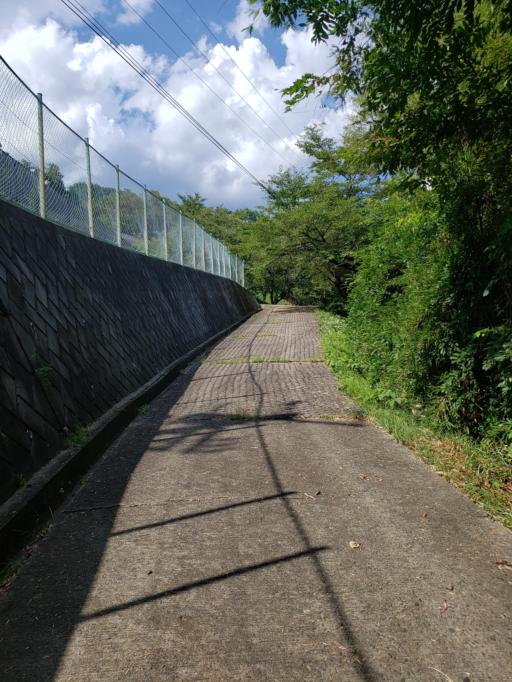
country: JP
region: Nagano
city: Nagano-shi
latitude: 36.6090
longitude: 138.0319
